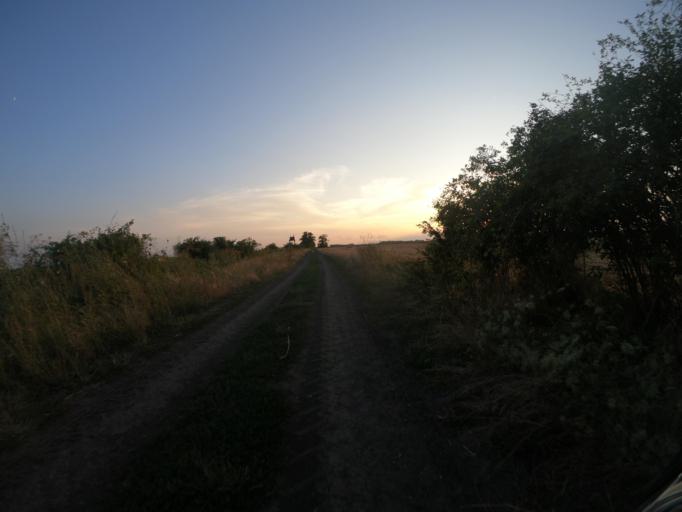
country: HU
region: Borsod-Abauj-Zemplen
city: Szentistvan
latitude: 47.7466
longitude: 20.7450
